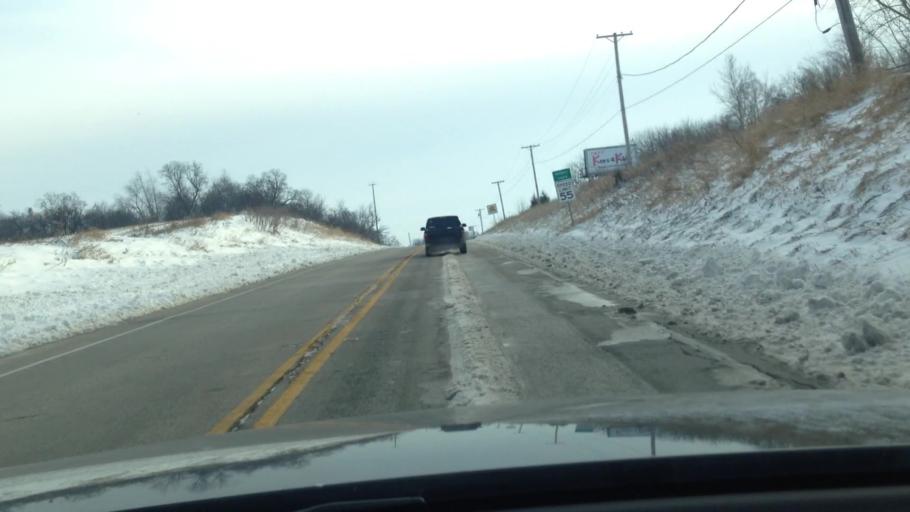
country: US
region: Illinois
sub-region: McHenry County
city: Hebron
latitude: 42.4938
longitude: -88.4424
